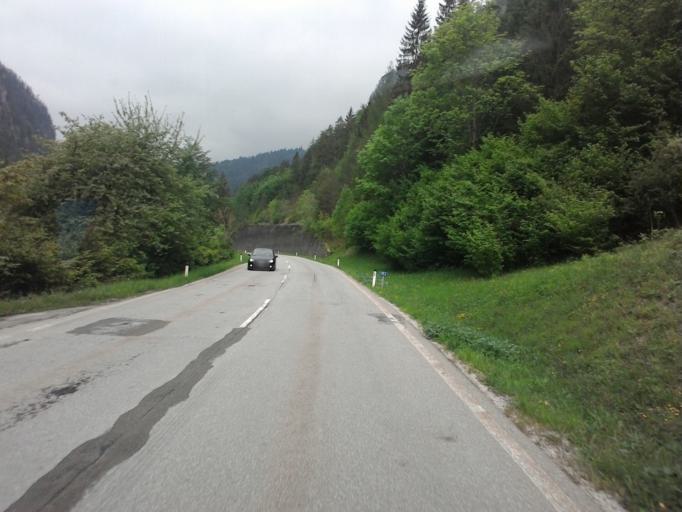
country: AT
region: Styria
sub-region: Politischer Bezirk Liezen
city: Palfau
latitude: 47.7091
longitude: 14.8496
